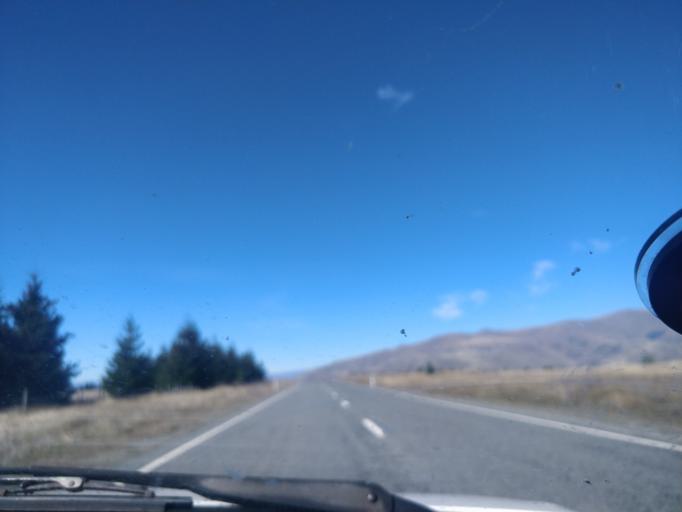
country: NZ
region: Otago
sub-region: Queenstown-Lakes District
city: Wanaka
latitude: -44.2696
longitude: 170.0429
